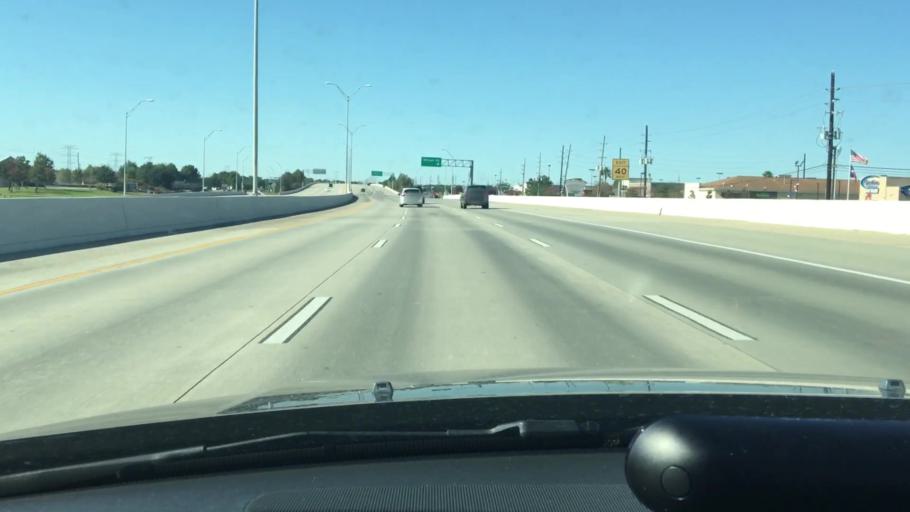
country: US
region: Texas
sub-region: Harris County
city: Humble
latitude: 29.9348
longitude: -95.2422
